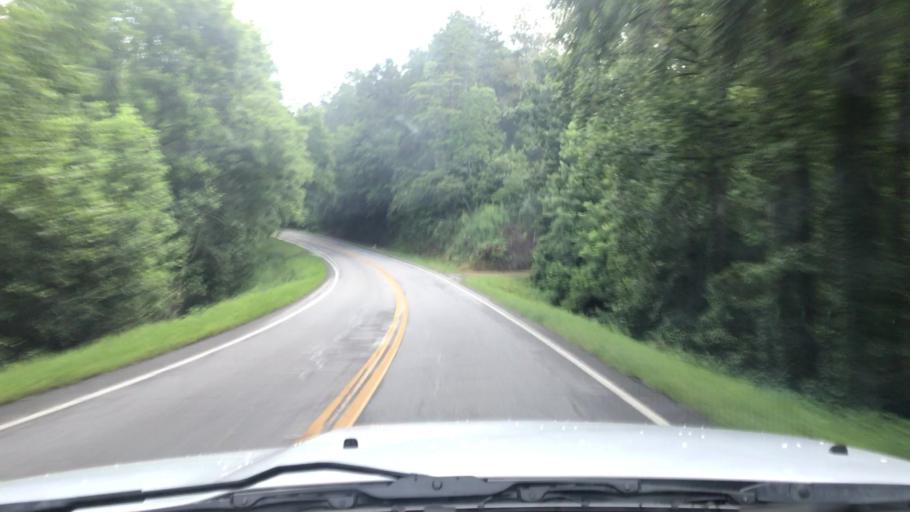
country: US
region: Georgia
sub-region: Fannin County
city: Blue Ridge
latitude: 34.9234
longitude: -84.2701
